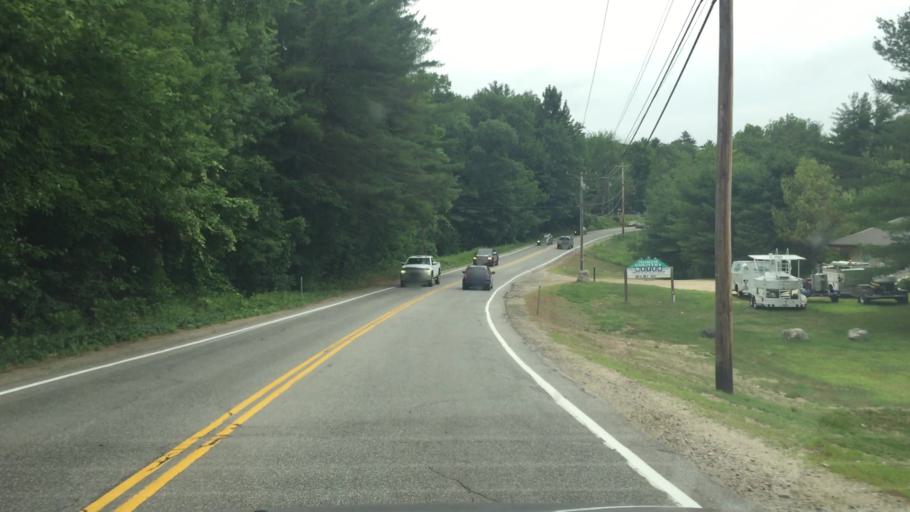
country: US
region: New Hampshire
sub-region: Carroll County
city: Center Harbor
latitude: 43.7255
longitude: -71.4306
